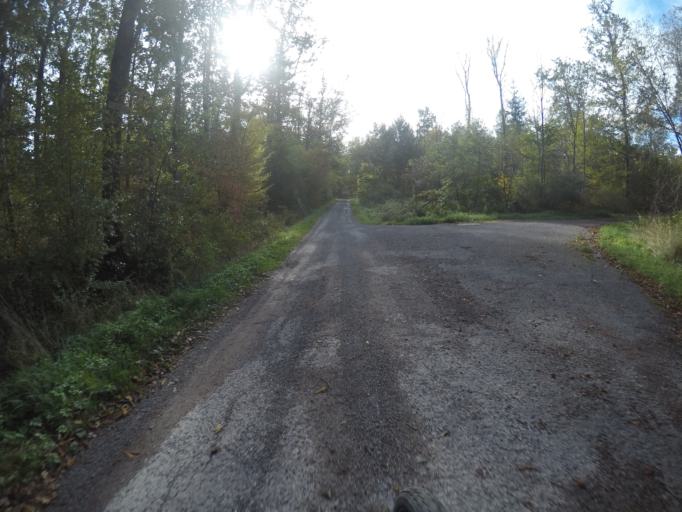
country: DE
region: Baden-Wuerttemberg
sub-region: Regierungsbezirk Stuttgart
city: Ehningen
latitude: 48.6759
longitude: 8.9580
